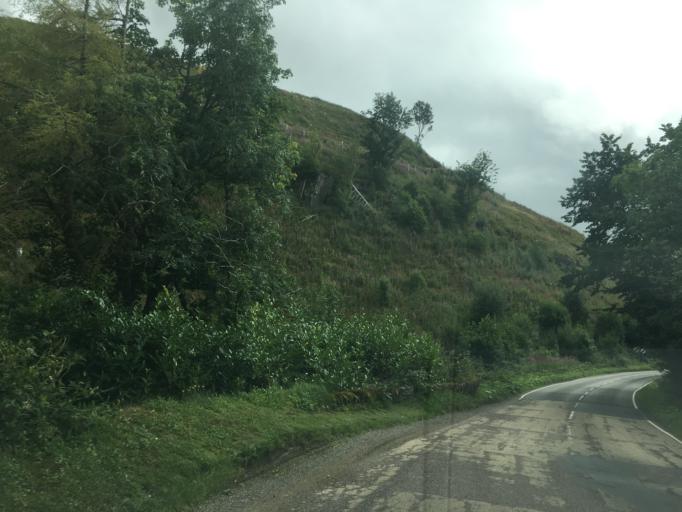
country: GB
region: Scotland
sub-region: Argyll and Bute
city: Lochgilphead
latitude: 56.1325
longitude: -5.4838
